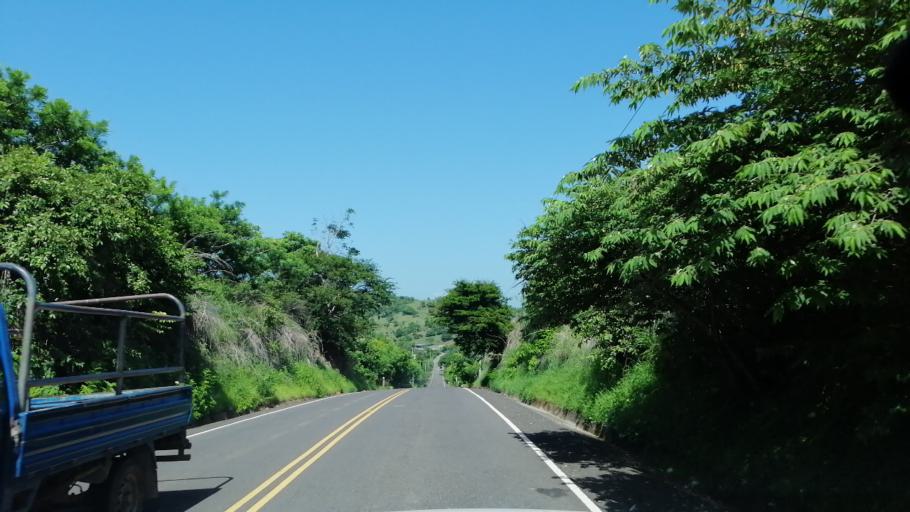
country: HN
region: Lempira
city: La Virtud
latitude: 13.9878
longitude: -88.7472
